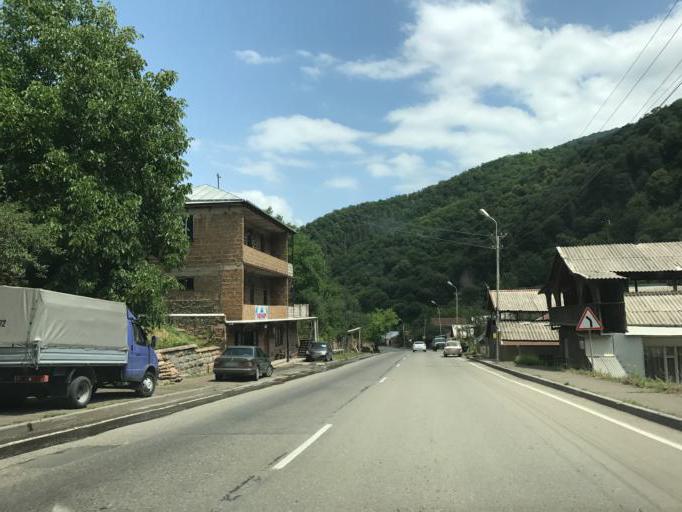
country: AM
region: Tavush
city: Dilijan
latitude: 40.7243
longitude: 44.8637
